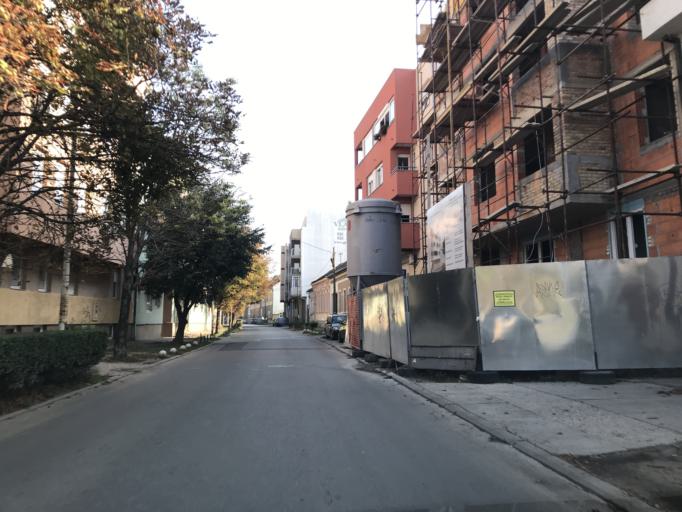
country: RS
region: Autonomna Pokrajina Vojvodina
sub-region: Juznobacki Okrug
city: Novi Sad
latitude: 45.2518
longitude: 19.8311
